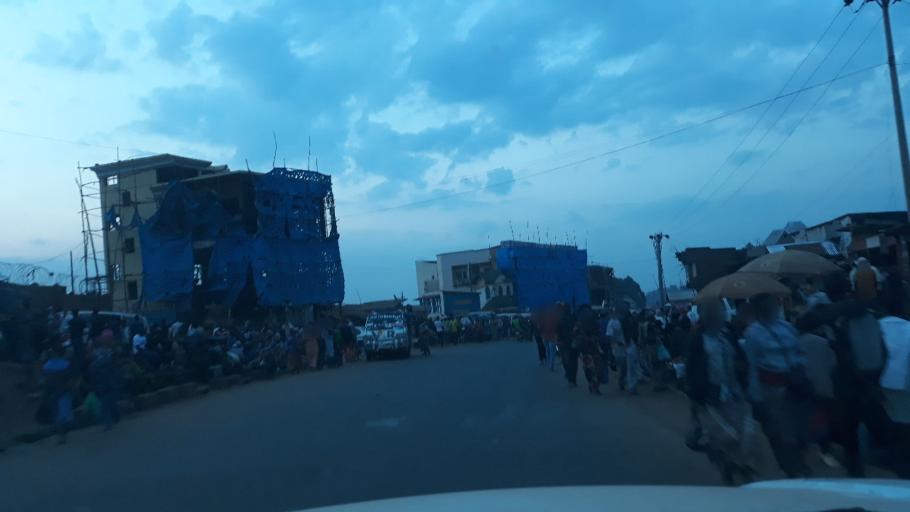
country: CD
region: South Kivu
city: Bukavu
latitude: -2.5243
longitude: 28.8537
